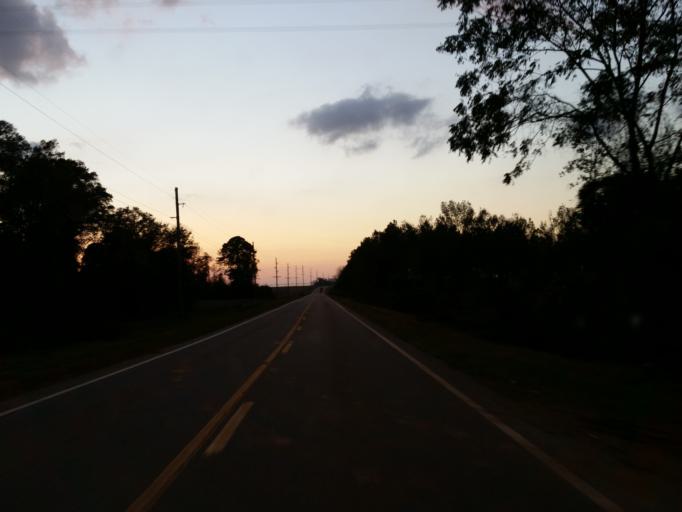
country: US
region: Georgia
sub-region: Dooly County
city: Vienna
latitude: 32.1235
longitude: -83.7320
